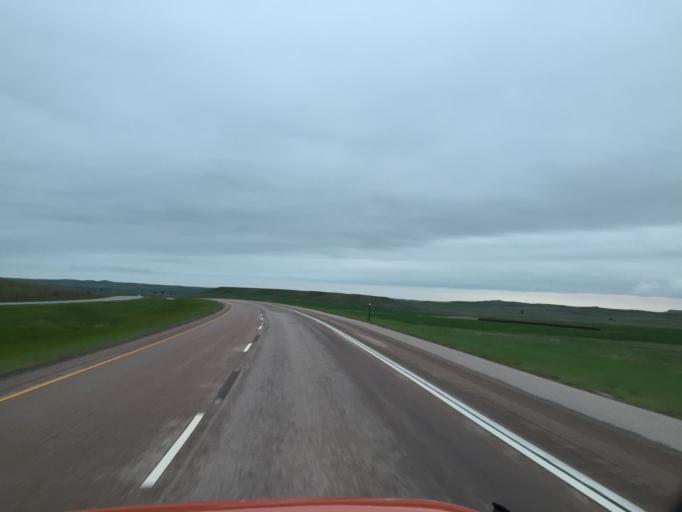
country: US
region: South Dakota
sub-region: Pennington County
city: Colonial Pine Hills
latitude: 43.7031
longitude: -103.2315
